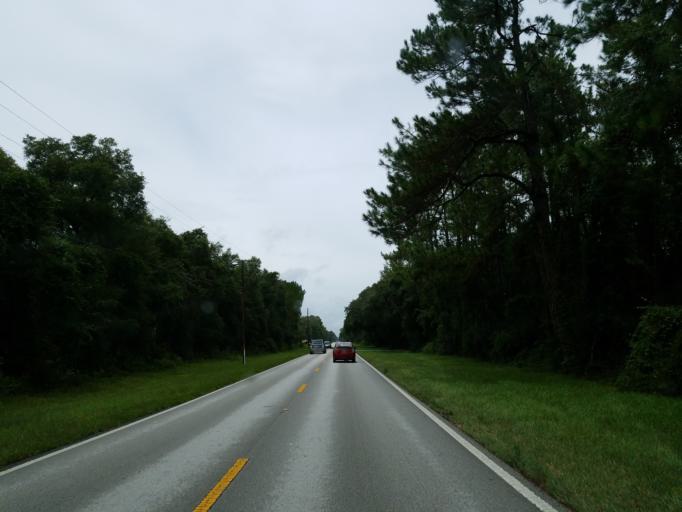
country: US
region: Florida
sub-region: Citrus County
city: Floral City
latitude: 28.6996
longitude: -82.2186
